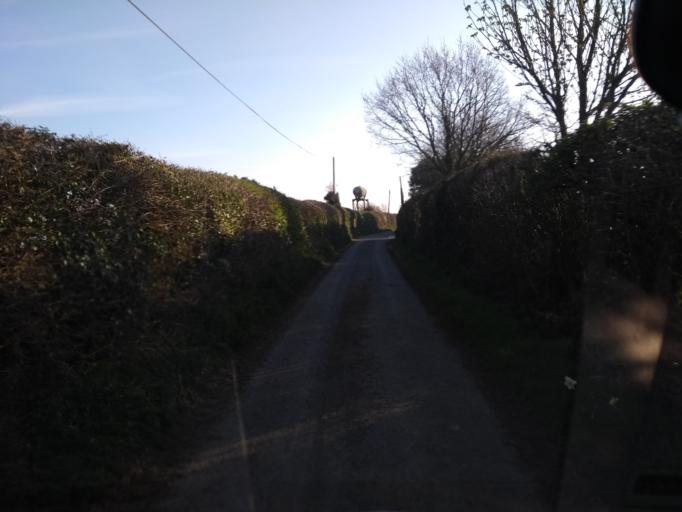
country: GB
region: England
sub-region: Somerset
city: Crewkerne
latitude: 50.8615
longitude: -2.8123
